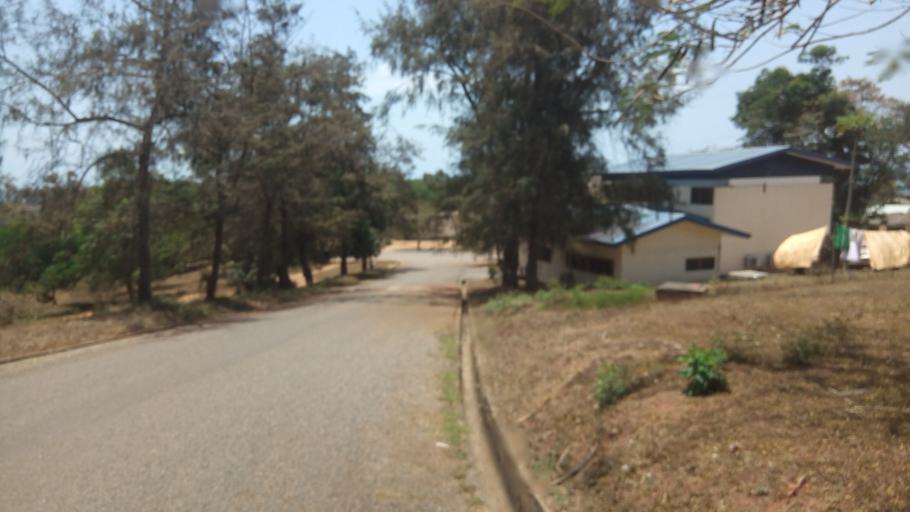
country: GH
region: Central
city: Cape Coast
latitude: 5.1057
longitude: -1.2814
